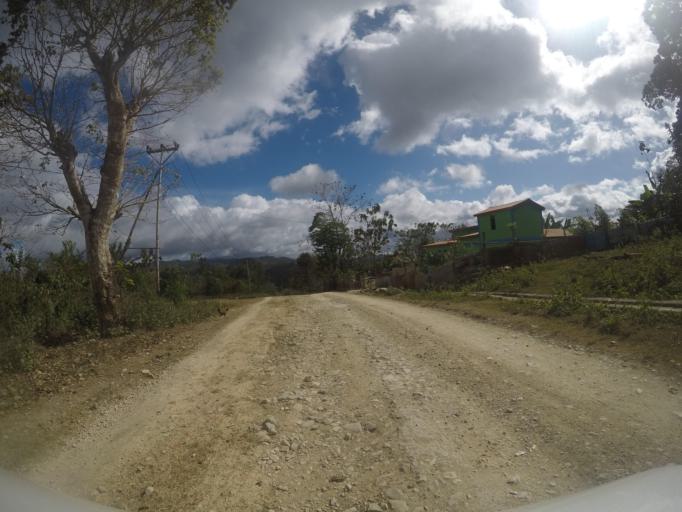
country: TL
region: Lautem
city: Lospalos
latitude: -8.5527
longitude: 126.8974
